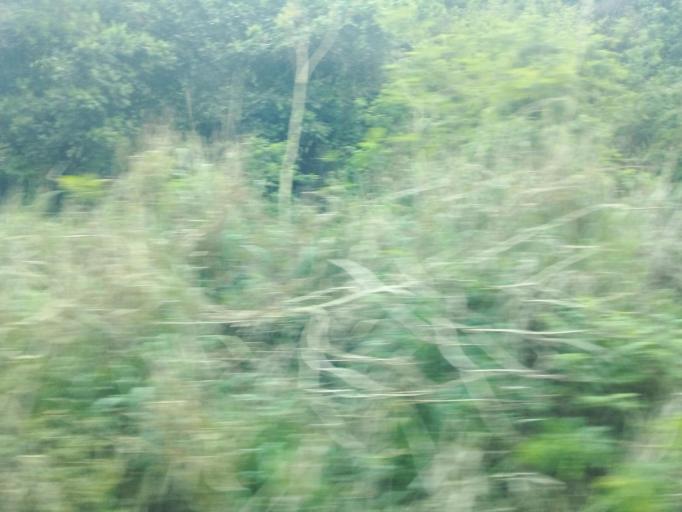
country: BR
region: Minas Gerais
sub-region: Ipaba
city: Ipaba
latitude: -19.4626
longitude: -42.4516
